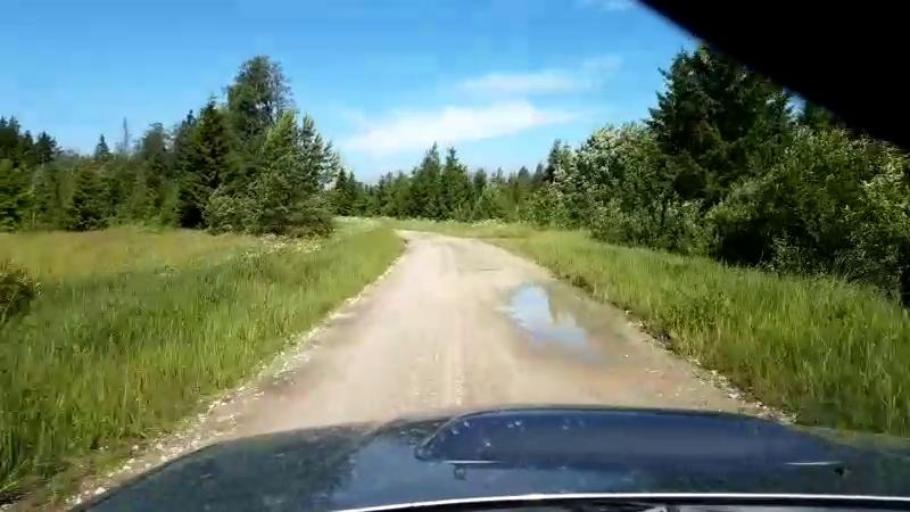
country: EE
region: Paernumaa
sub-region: Sindi linn
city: Sindi
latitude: 58.5090
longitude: 24.6906
